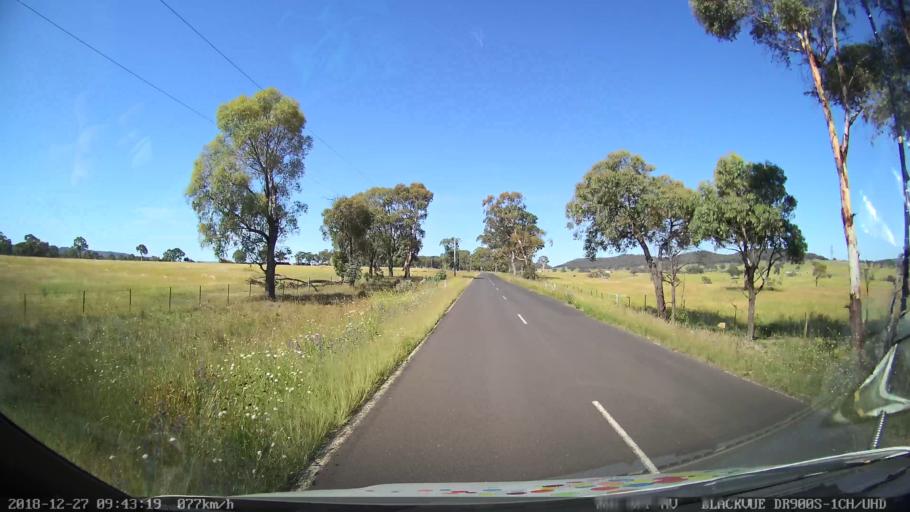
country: AU
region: New South Wales
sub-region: Lithgow
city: Portland
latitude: -33.3053
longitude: 150.0022
